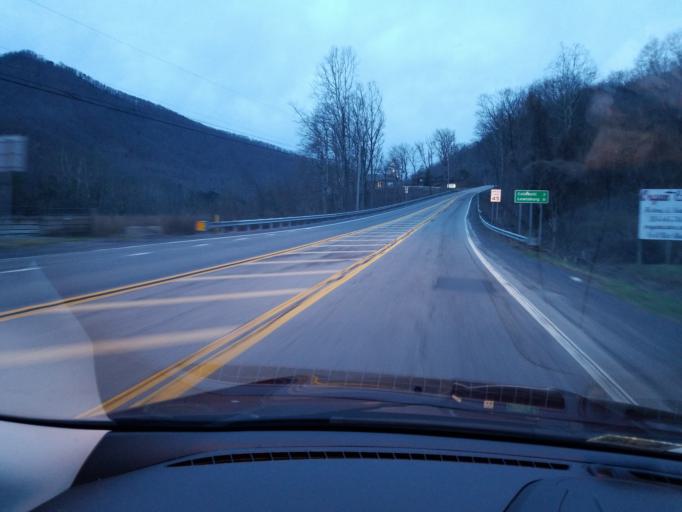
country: US
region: West Virginia
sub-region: Greenbrier County
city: White Sulphur Springs
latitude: 37.7726
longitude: -80.3572
